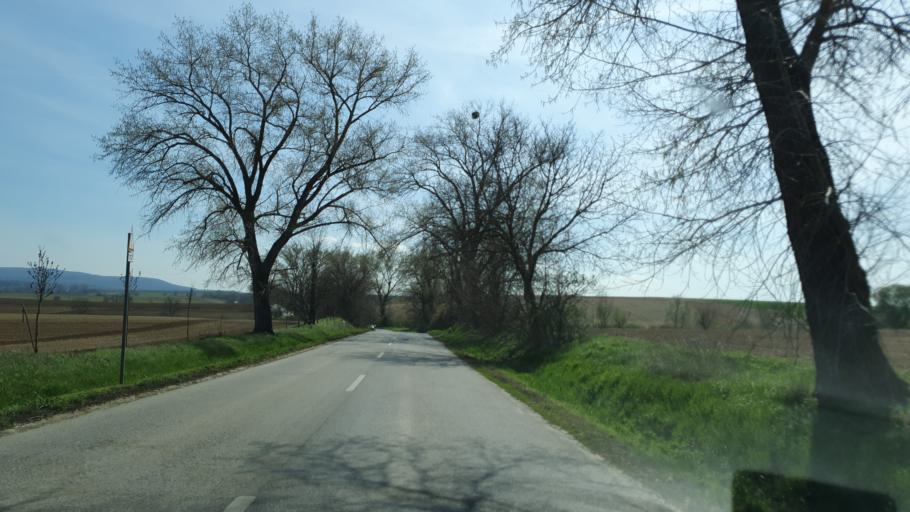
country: HU
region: Komarom-Esztergom
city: Bokod
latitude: 47.4869
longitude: 18.2411
